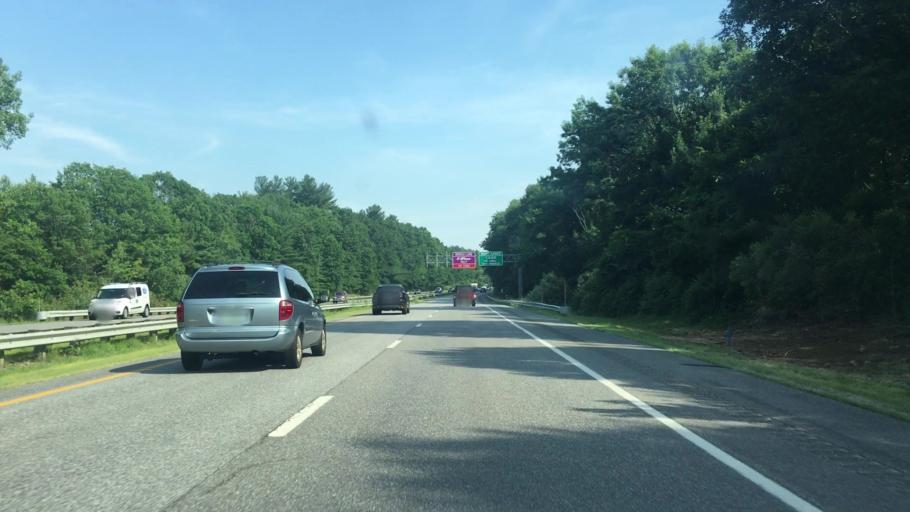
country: US
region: New Hampshire
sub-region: Strafford County
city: Dover
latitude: 43.1613
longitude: -70.8524
